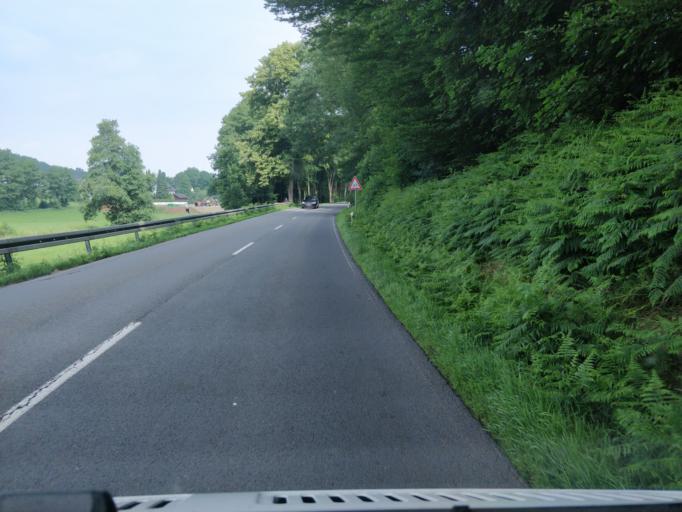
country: DE
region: North Rhine-Westphalia
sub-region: Regierungsbezirk Koln
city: Numbrecht
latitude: 50.9095
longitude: 7.5884
